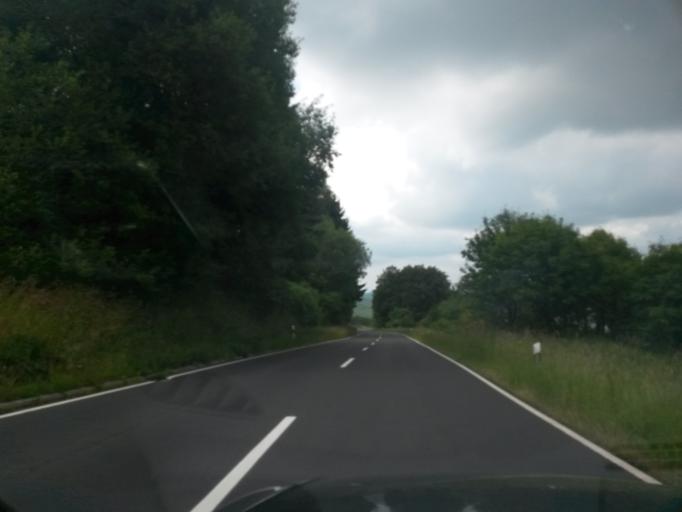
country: DE
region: Hesse
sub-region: Regierungsbezirk Kassel
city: Gersfeld
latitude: 50.5051
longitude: 9.9448
